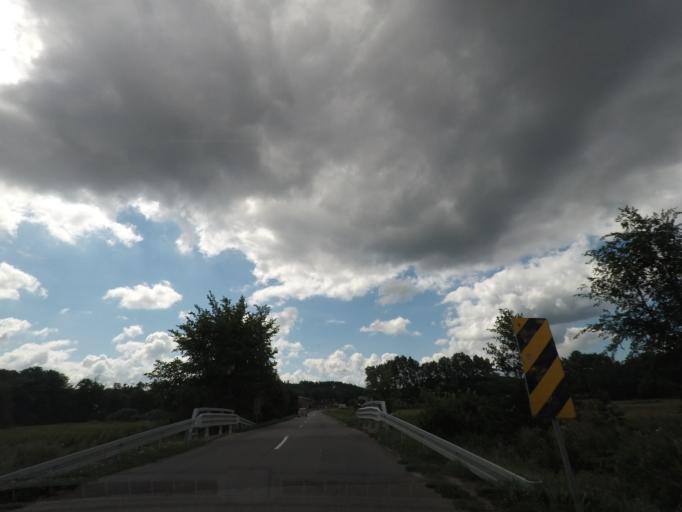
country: PL
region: Pomeranian Voivodeship
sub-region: Powiat wejherowski
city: Leczyce
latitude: 54.5783
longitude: 17.8655
